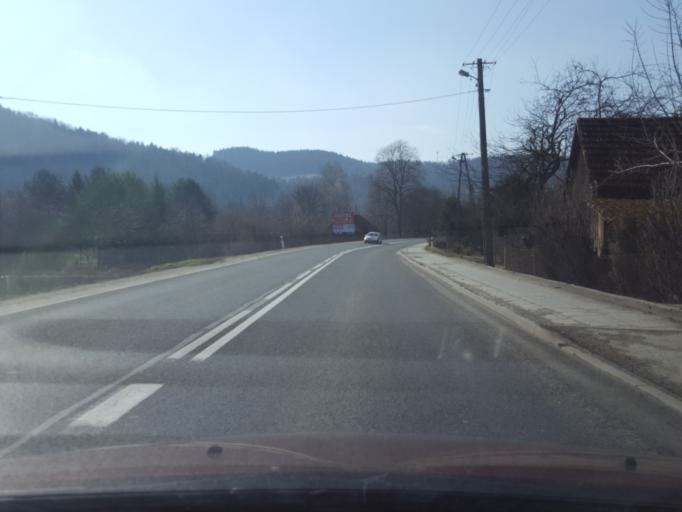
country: PL
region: Lesser Poland Voivodeship
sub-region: Powiat brzeski
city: Czchow
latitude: 49.8154
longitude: 20.6811
